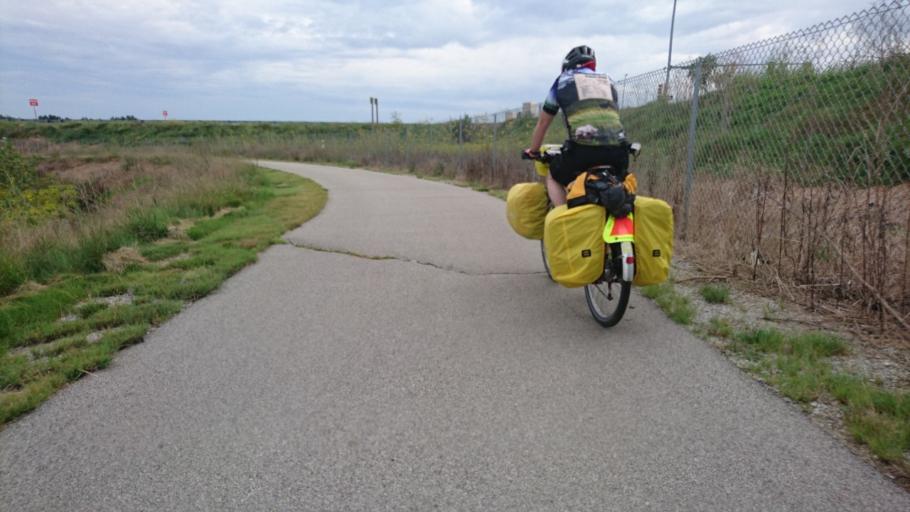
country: US
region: Illinois
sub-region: Sangamon County
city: Southern View
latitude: 39.7425
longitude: -89.6714
